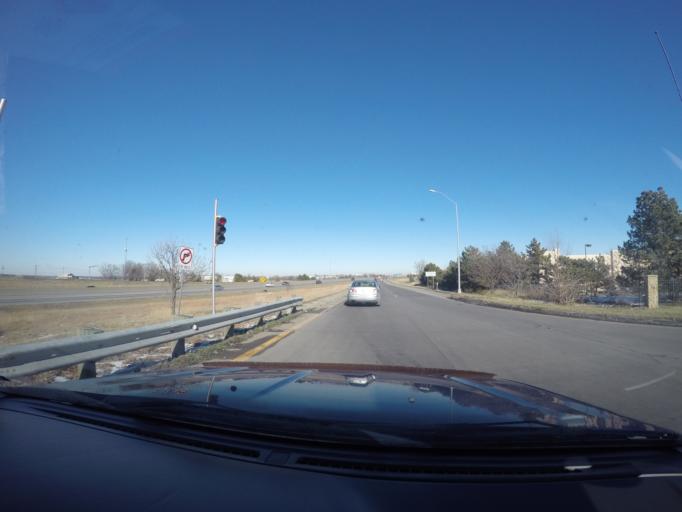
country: US
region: Kansas
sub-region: Johnson County
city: Lenexa
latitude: 38.9133
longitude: -94.7695
